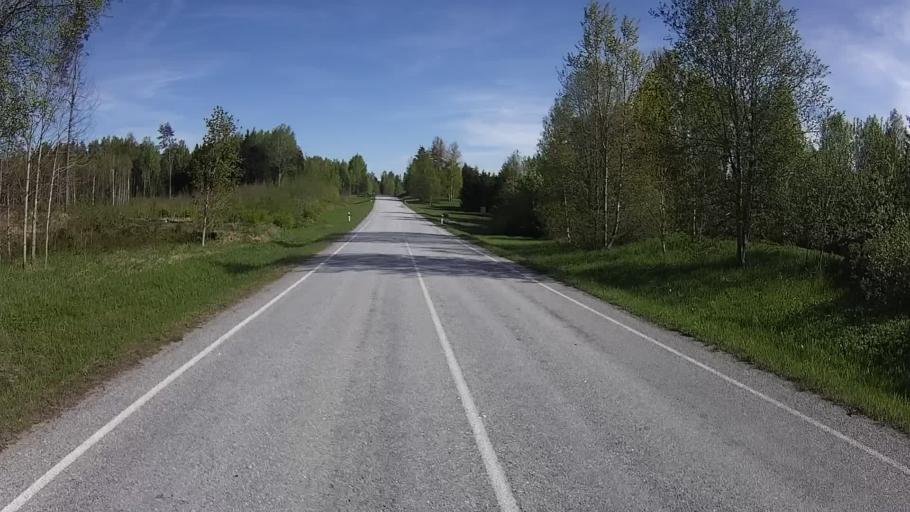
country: EE
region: Vorumaa
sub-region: Antsla vald
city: Vana-Antsla
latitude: 58.0087
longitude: 26.4960
